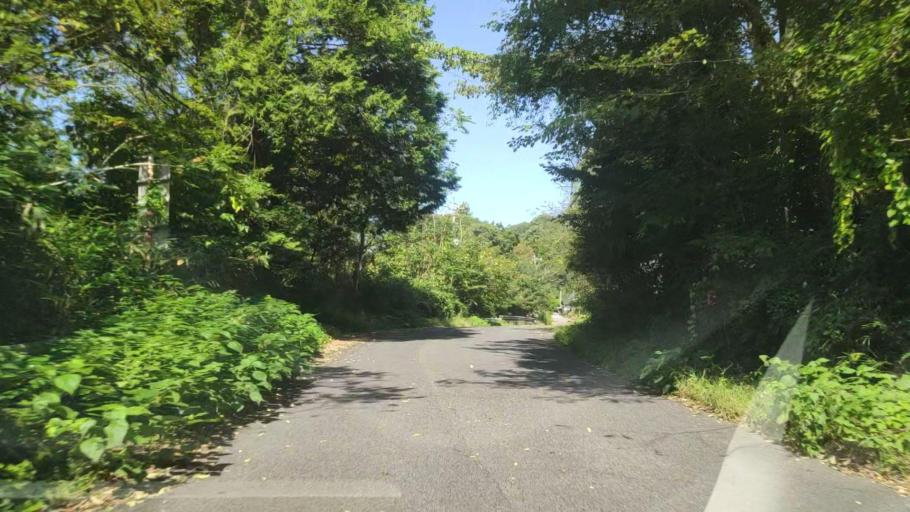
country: JP
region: Gunma
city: Numata
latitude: 36.5869
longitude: 139.0586
